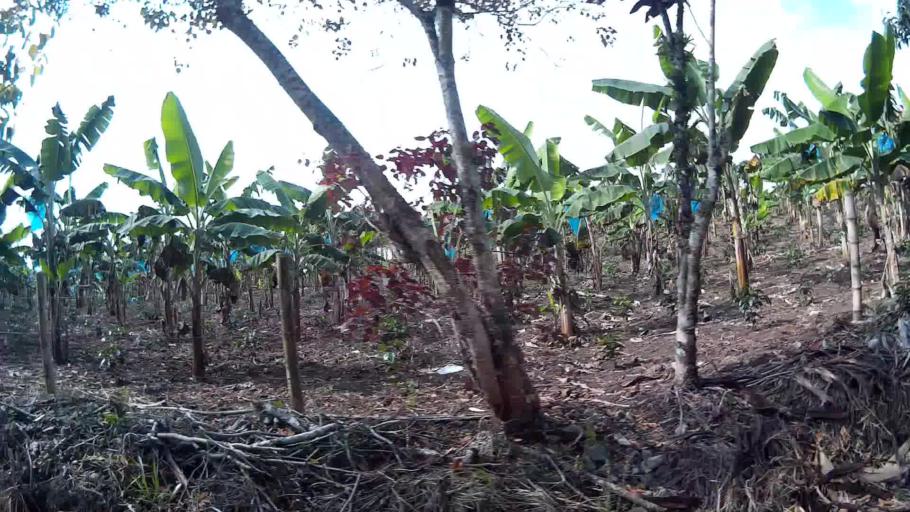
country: CO
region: Valle del Cauca
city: Ulloa
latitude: 4.7104
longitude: -75.6980
